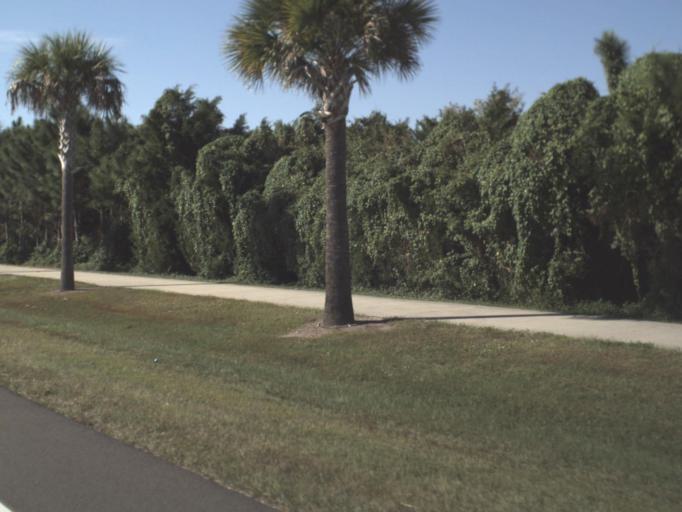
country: US
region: Florida
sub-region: Brevard County
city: South Patrick Shores
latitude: 28.1931
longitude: -80.7022
